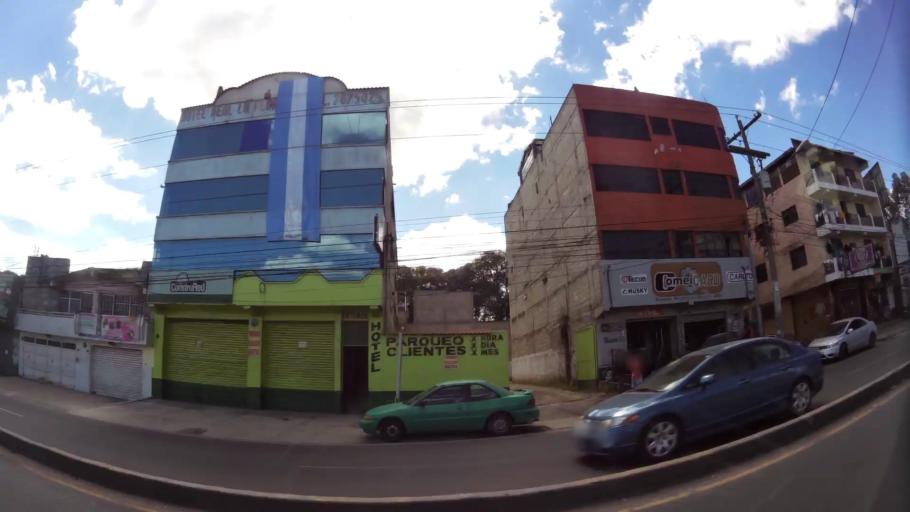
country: GT
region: Quetzaltenango
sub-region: Municipio de La Esperanza
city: La Esperanza
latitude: 14.8567
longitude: -91.5385
